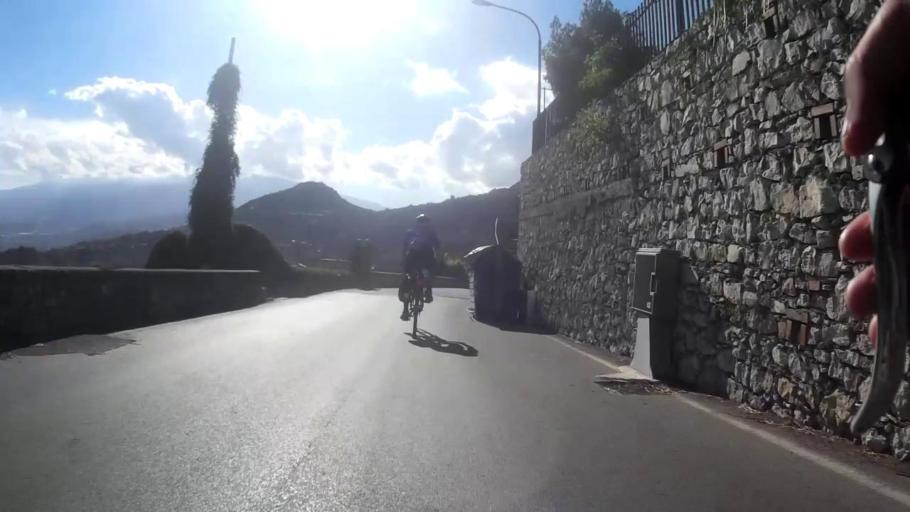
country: IT
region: Sicily
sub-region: Messina
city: Castelmola
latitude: 37.8550
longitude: 15.2816
